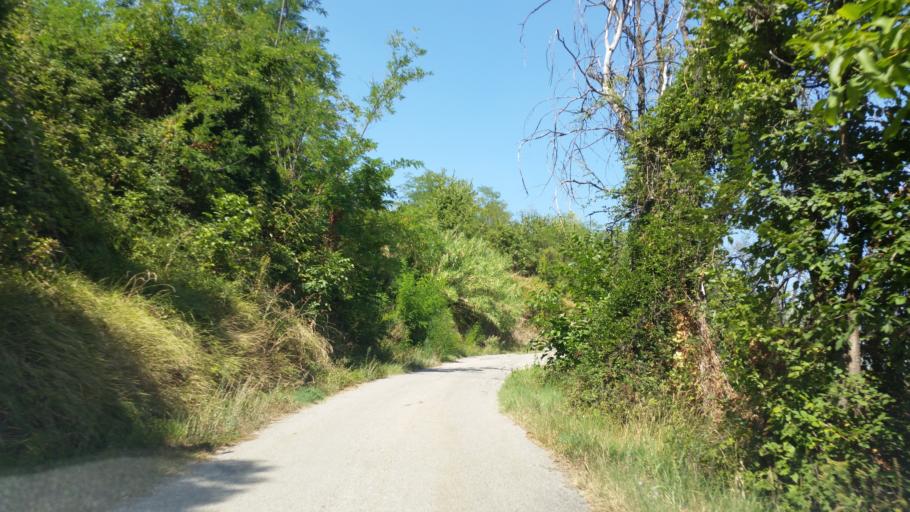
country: IT
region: Piedmont
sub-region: Provincia di Cuneo
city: Trezzo Tinella
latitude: 44.6769
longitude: 8.1007
